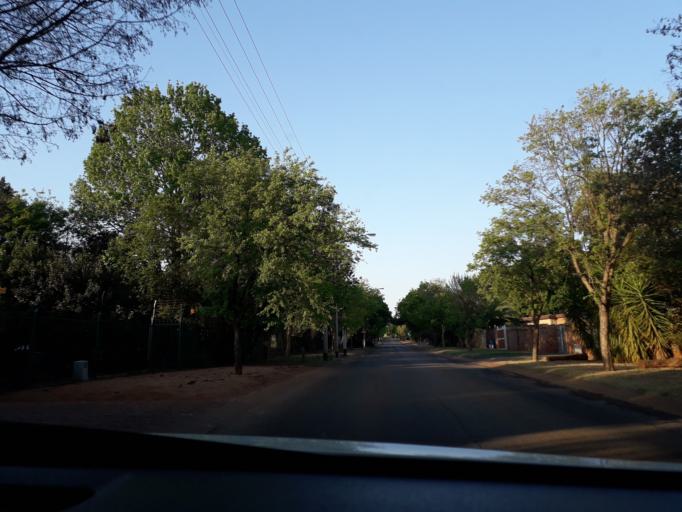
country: ZA
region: Gauteng
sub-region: City of Tshwane Metropolitan Municipality
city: Centurion
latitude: -25.8604
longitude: 28.2019
